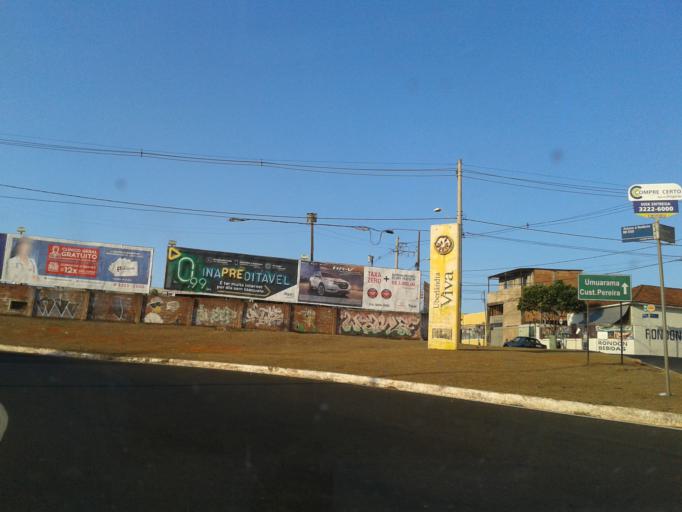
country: BR
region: Minas Gerais
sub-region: Uberlandia
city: Uberlandia
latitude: -18.8932
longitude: -48.2506
